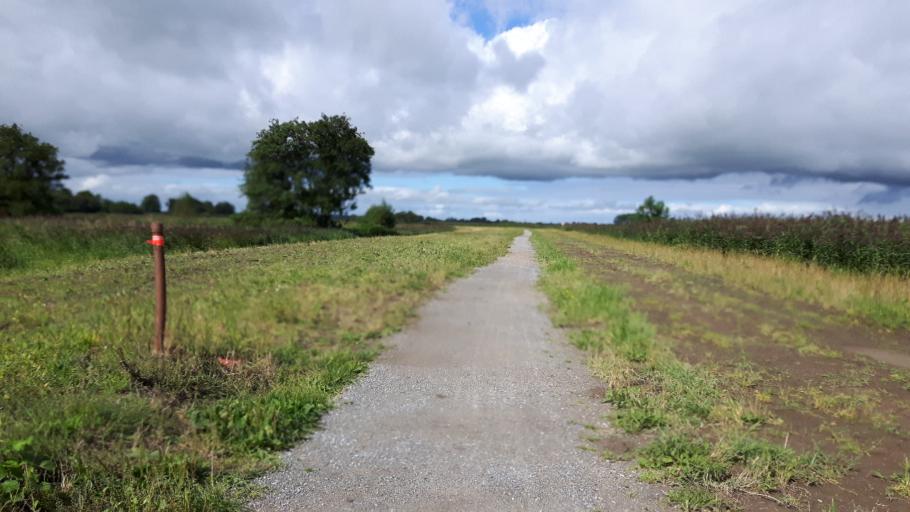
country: NL
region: Groningen
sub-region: Gemeente Slochteren
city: Slochteren
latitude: 53.2675
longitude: 6.8214
